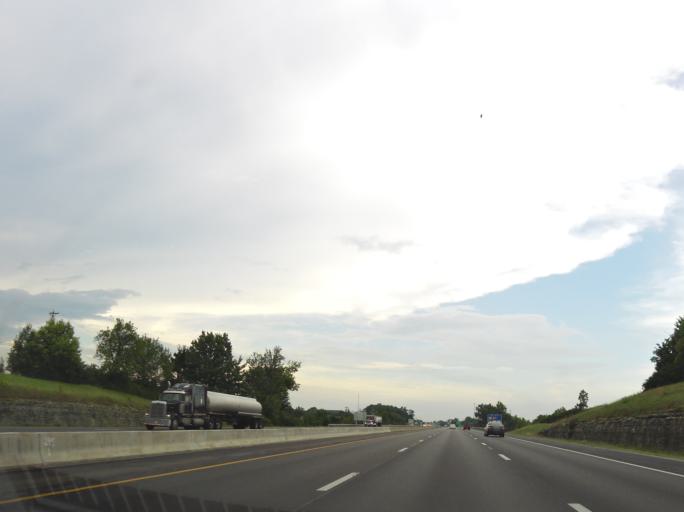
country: US
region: Kentucky
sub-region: Madison County
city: Richmond
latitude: 37.7482
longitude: -84.3211
